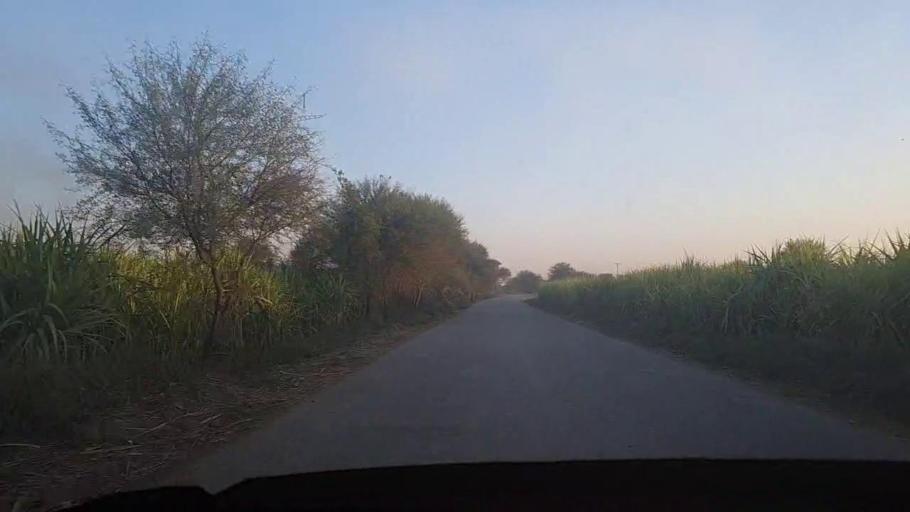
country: PK
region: Sindh
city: Sobhadero
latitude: 27.3421
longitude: 68.3782
